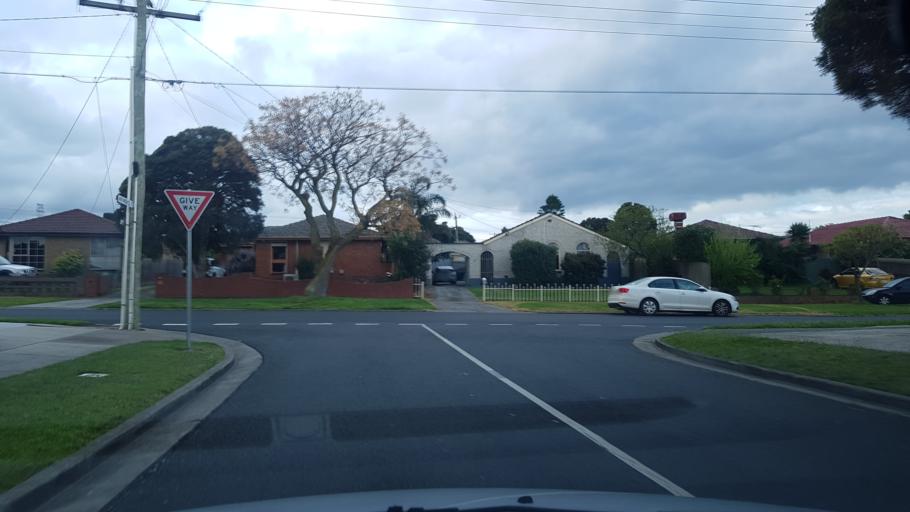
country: AU
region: Victoria
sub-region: Greater Dandenong
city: Springvale
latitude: -37.9456
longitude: 145.1350
